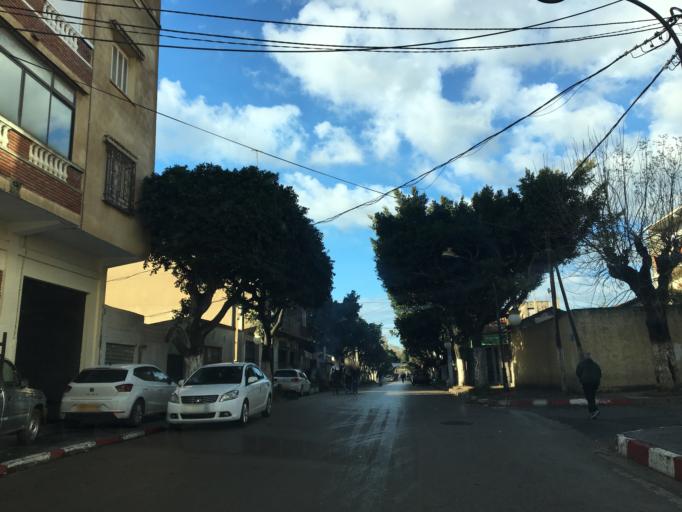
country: DZ
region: Tipaza
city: Tipasa
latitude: 36.5687
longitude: 2.3951
